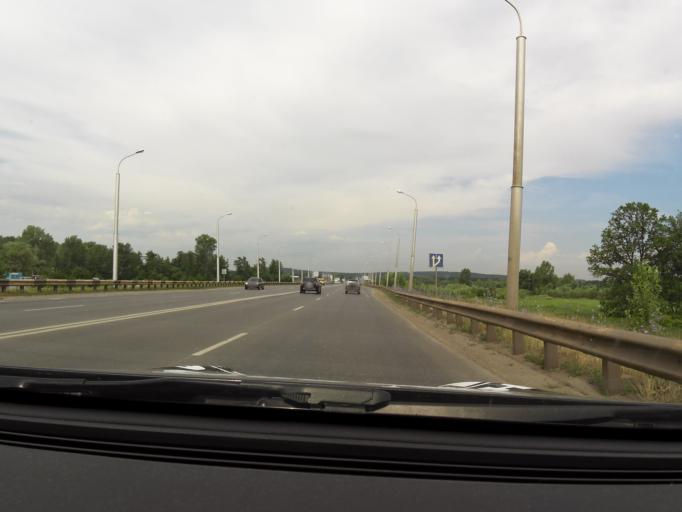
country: RU
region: Bashkortostan
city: Ufa
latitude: 54.8039
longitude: 56.1859
